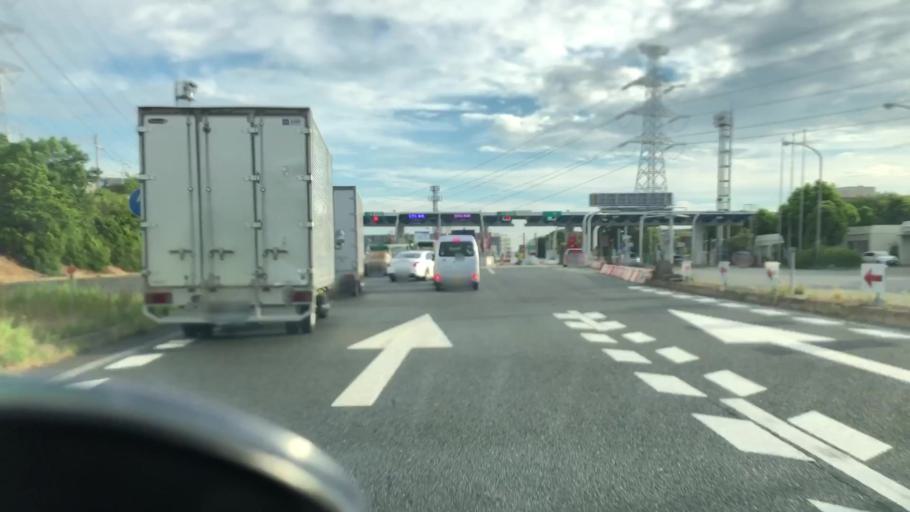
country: JP
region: Hyogo
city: Takarazuka
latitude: 34.8059
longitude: 135.3687
